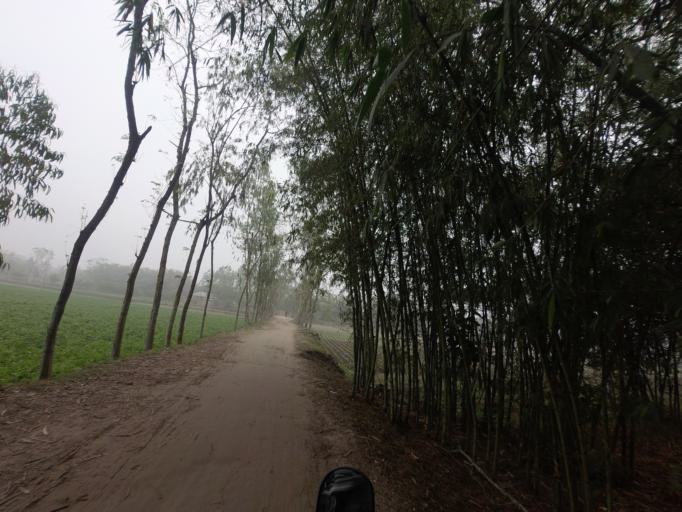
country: BD
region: Rajshahi
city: Saidpur
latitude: 26.0361
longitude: 88.8702
